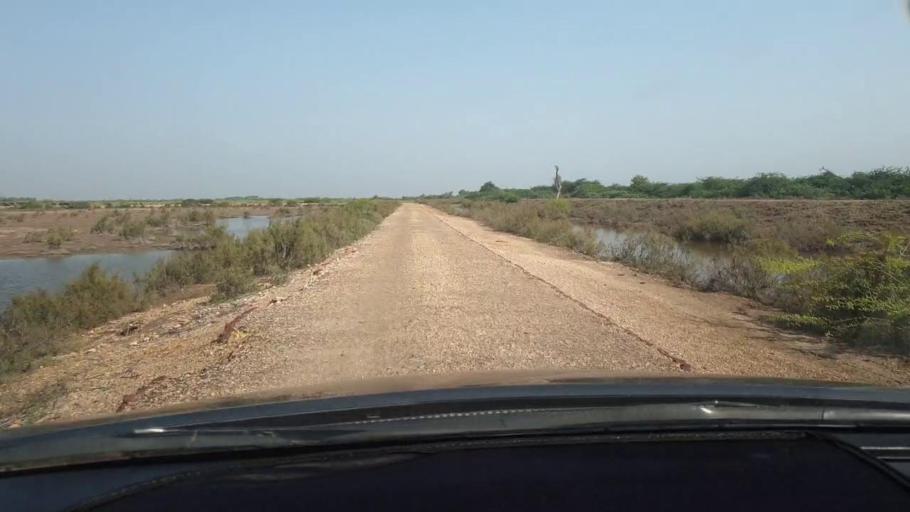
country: PK
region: Sindh
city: Tando Bago
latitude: 24.6778
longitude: 69.1689
